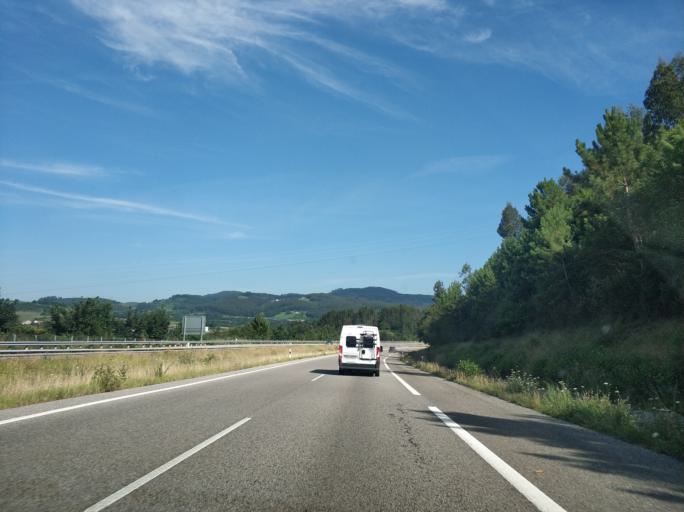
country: ES
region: Asturias
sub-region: Province of Asturias
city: Muros de Nalon
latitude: 43.5269
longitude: -6.0945
